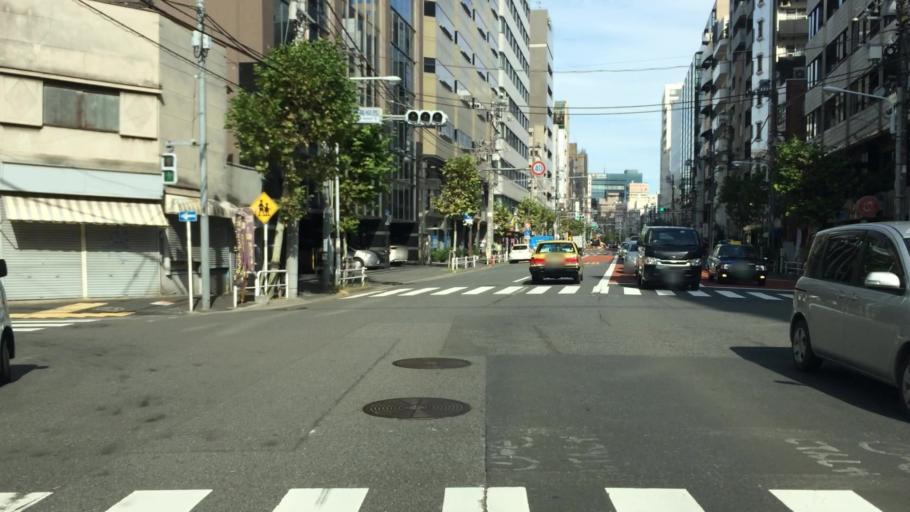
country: JP
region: Tokyo
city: Tokyo
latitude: 35.7085
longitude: 139.7821
